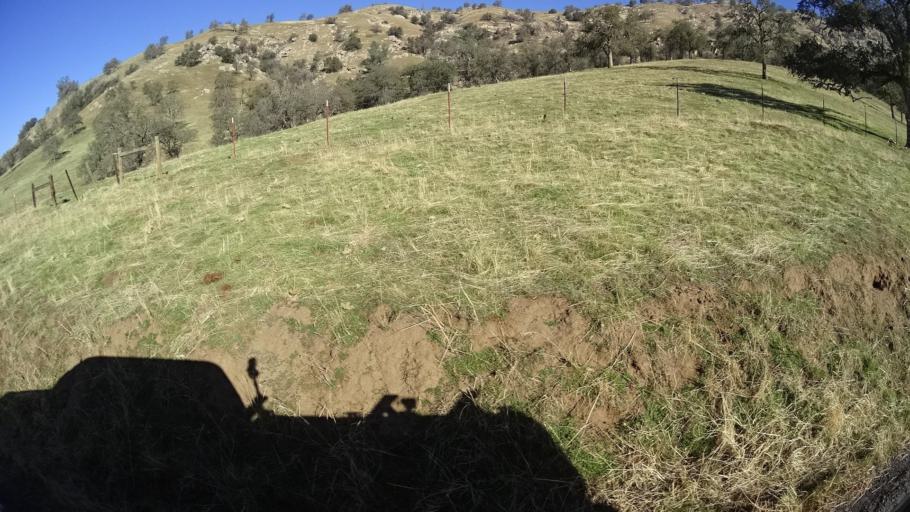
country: US
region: California
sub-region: Kern County
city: Alta Sierra
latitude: 35.7903
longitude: -118.7981
